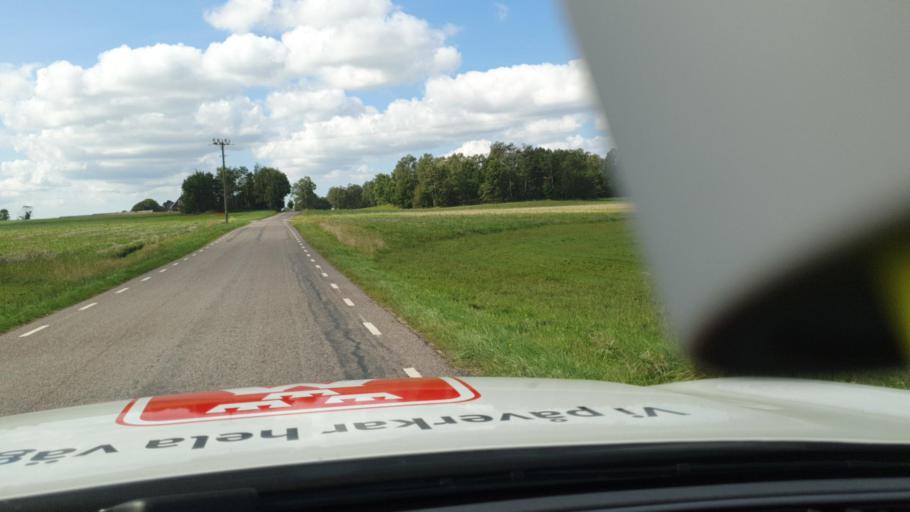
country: SE
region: Halland
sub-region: Laholms Kommun
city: Laholm
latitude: 56.4511
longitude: 13.1572
